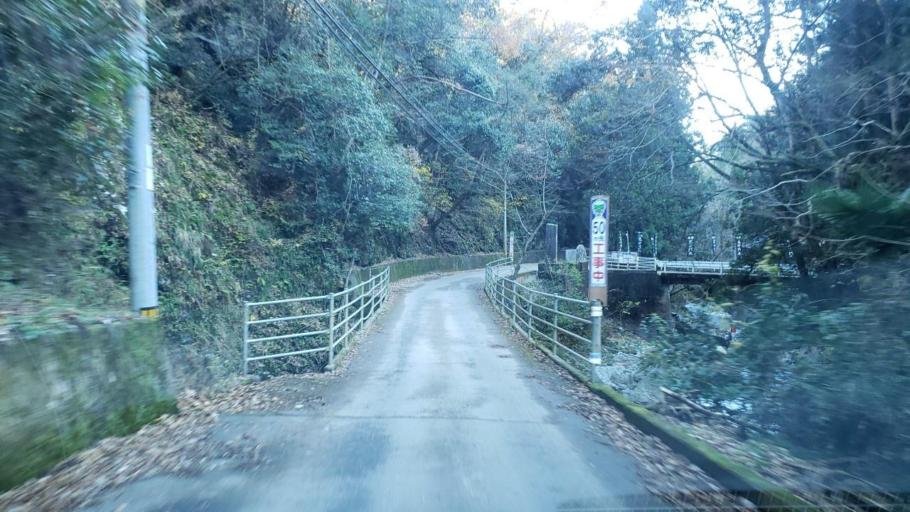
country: JP
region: Tokushima
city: Wakimachi
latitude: 33.9910
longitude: 133.9985
